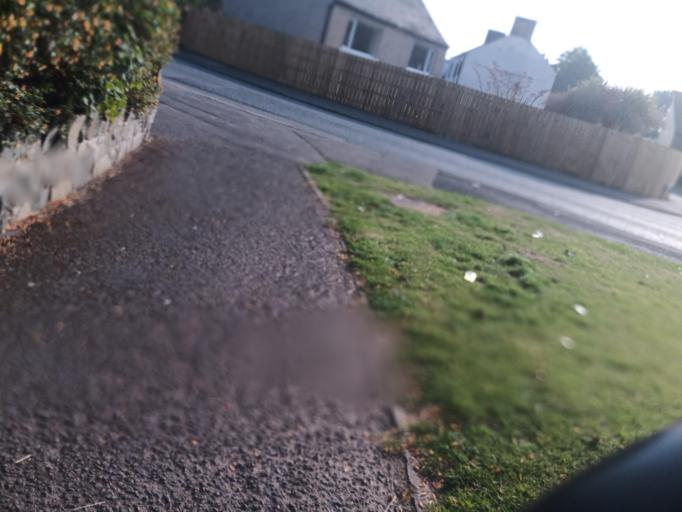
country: GB
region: Northern Ireland
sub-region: Ards District
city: Comber
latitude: 54.5517
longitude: -5.7426
